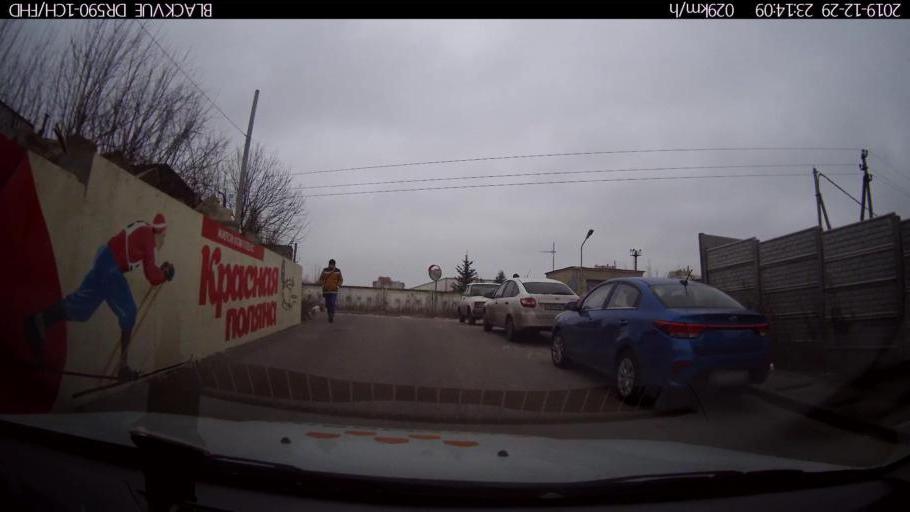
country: RU
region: Nizjnij Novgorod
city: Afonino
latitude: 56.2789
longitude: 44.0830
